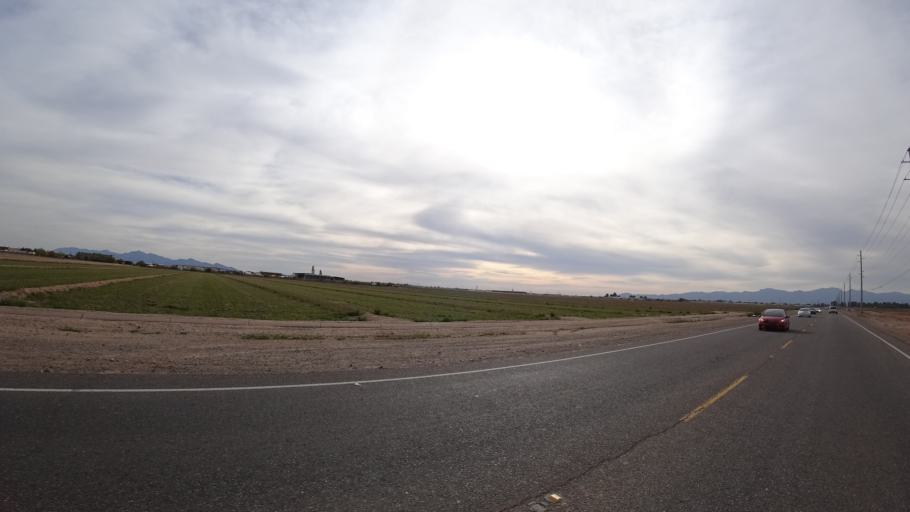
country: US
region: Arizona
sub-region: Maricopa County
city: Youngtown
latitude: 33.5655
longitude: -112.3304
